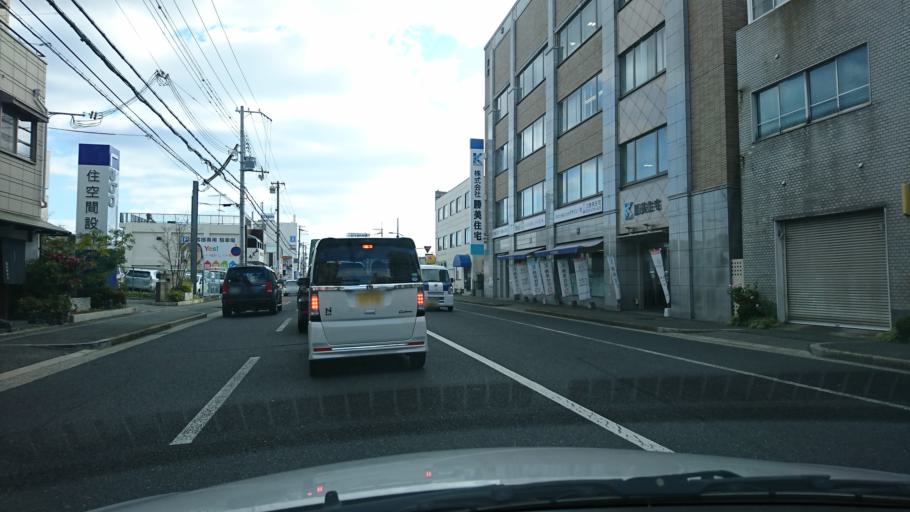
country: JP
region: Hyogo
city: Akashi
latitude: 34.6645
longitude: 134.9645
